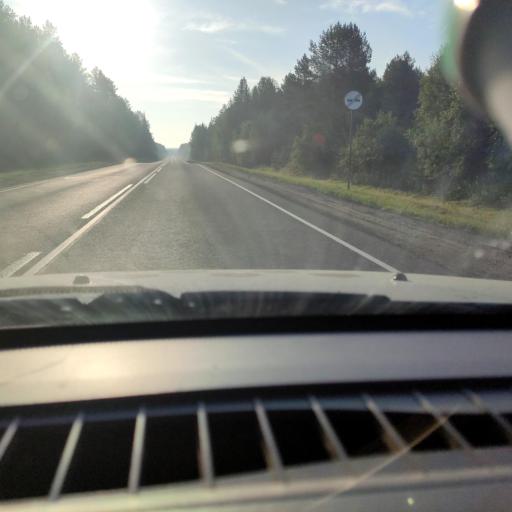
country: RU
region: Kirov
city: Dubrovka
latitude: 58.9055
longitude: 51.2191
